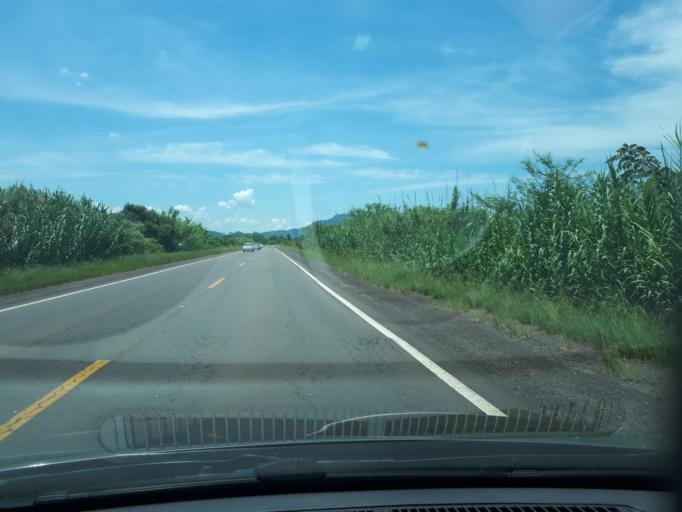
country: BR
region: Rio Grande do Sul
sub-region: Candelaria
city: Candelaria
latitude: -29.7264
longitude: -52.9322
